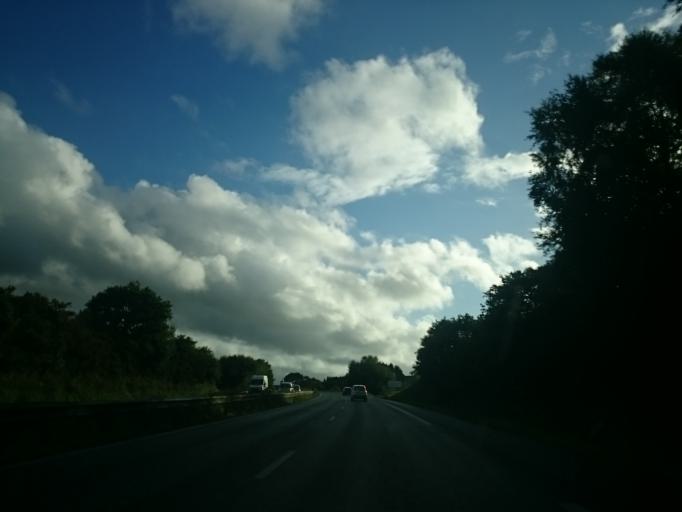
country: FR
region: Brittany
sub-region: Departement du Finistere
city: Morlaix
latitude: 48.5872
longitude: -3.8479
